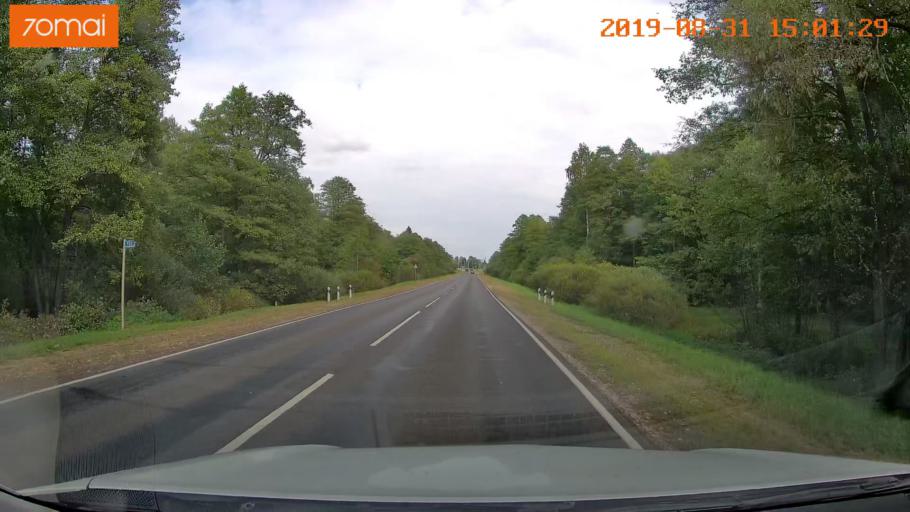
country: RU
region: Kaluga
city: Spas-Demensk
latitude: 54.3396
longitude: 34.0575
